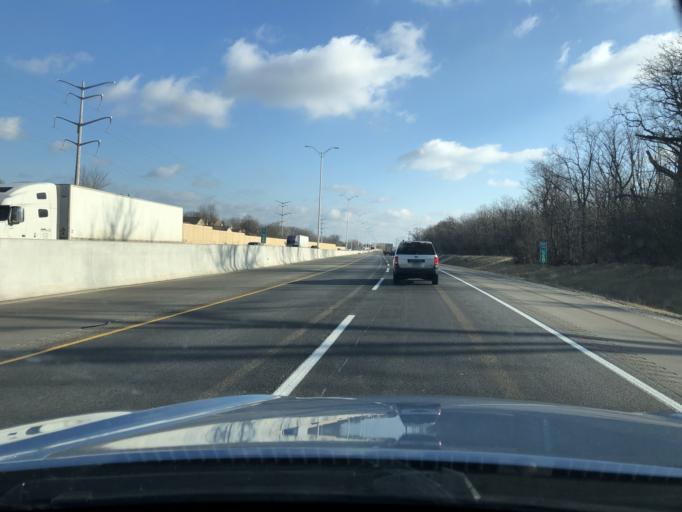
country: US
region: Illinois
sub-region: Cook County
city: Northbrook
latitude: 42.1442
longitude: -87.8267
